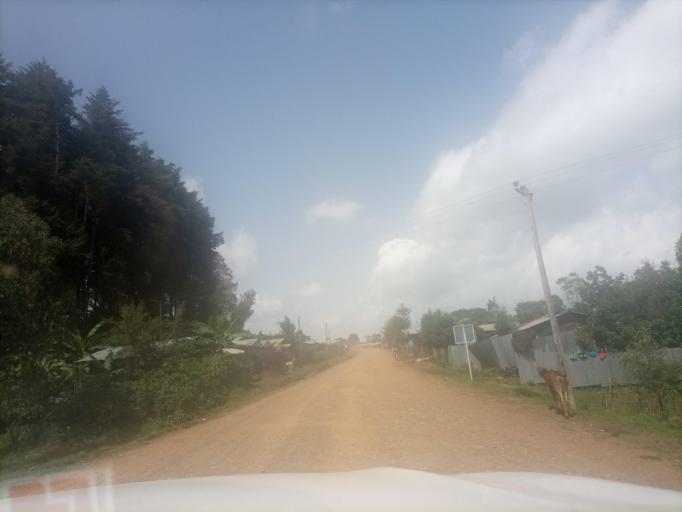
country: ET
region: Oromiya
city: Agaro
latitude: 7.7868
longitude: 36.4175
